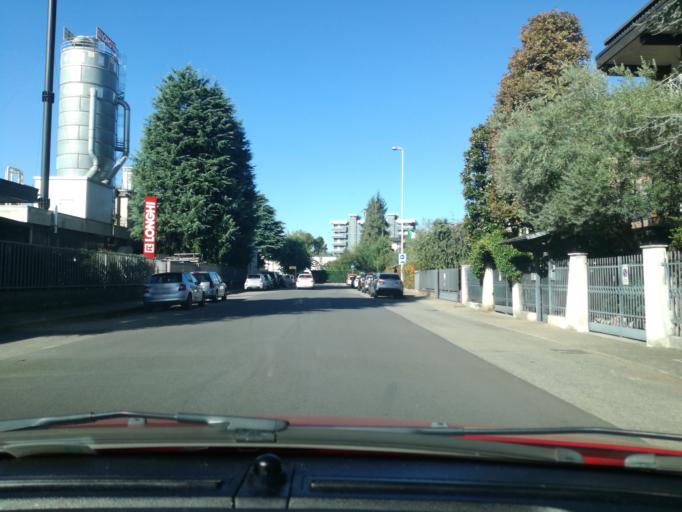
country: IT
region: Lombardy
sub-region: Provincia di Monza e Brianza
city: Meda
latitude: 45.6570
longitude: 9.1753
